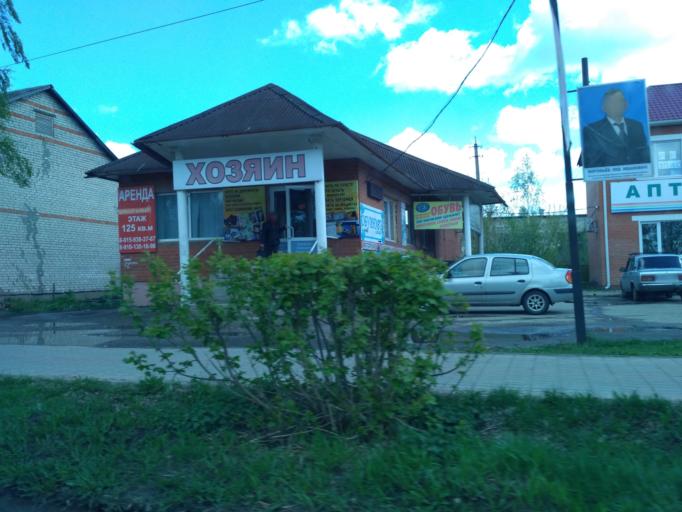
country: RU
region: Nizjnij Novgorod
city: Vad
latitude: 55.5316
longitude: 44.2109
